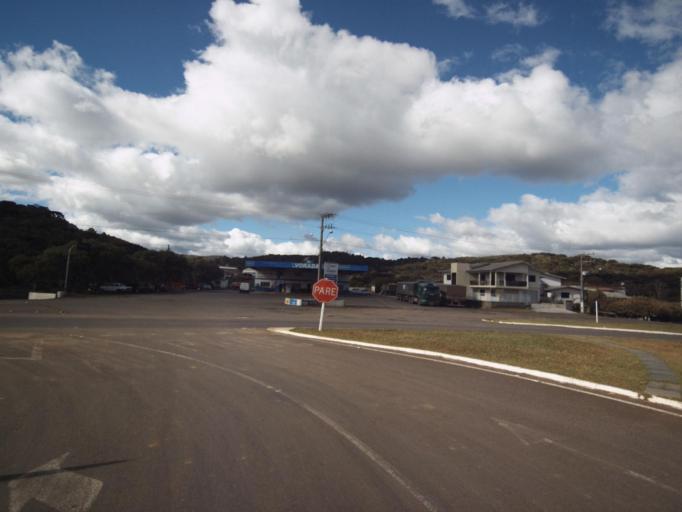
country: BR
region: Santa Catarina
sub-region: Joacaba
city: Joacaba
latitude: -27.0039
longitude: -51.7397
